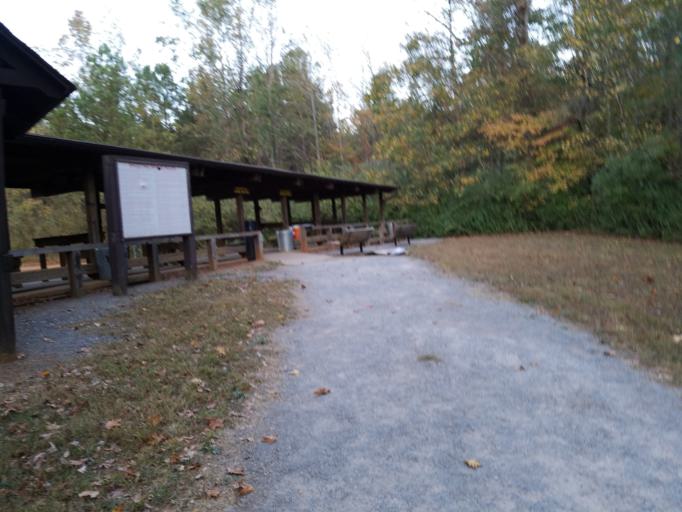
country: US
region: Georgia
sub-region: Gordon County
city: Calhoun
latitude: 34.6178
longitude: -85.0461
